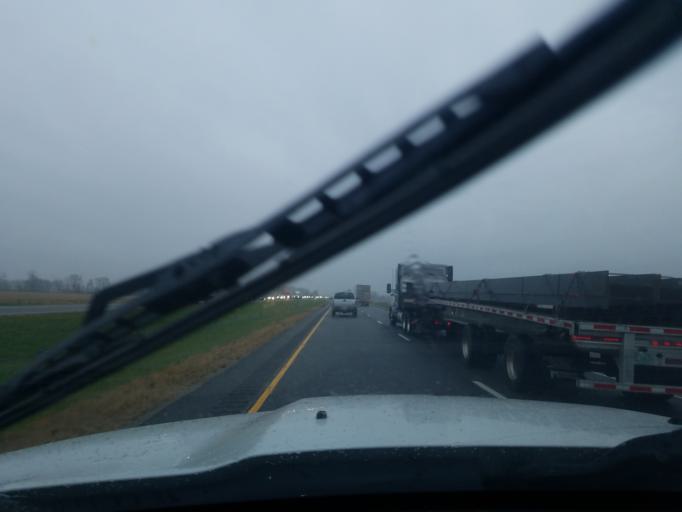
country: US
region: Indiana
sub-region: Grant County
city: Upland
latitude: 40.3985
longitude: -85.5489
